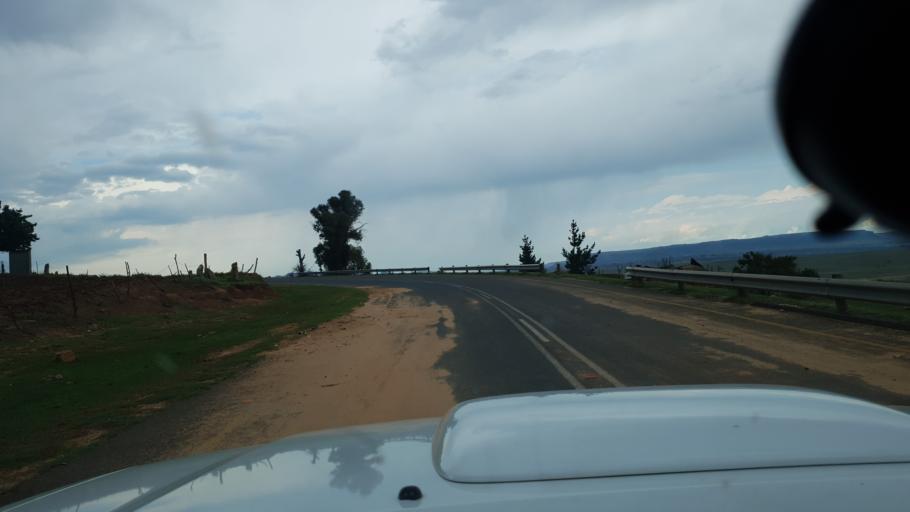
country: LS
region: Maseru
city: Maseru
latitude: -29.4592
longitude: 27.4906
